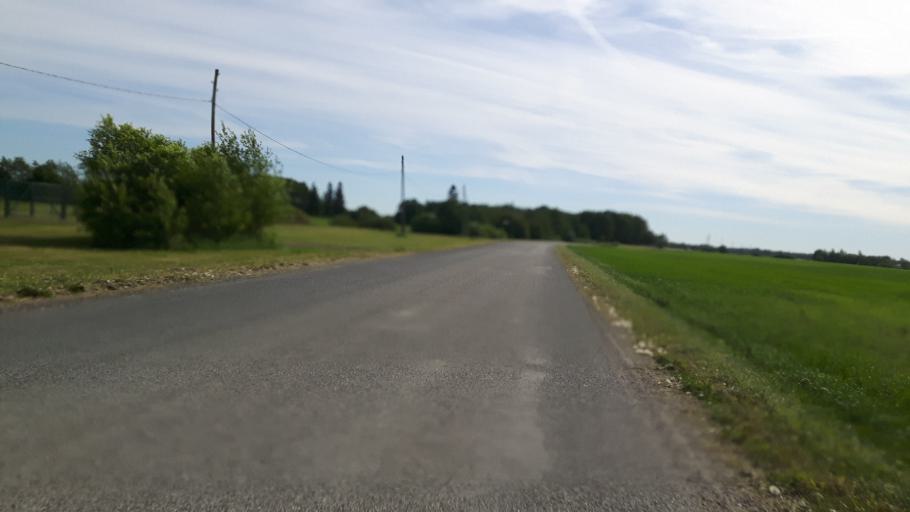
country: EE
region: Harju
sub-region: Raasiku vald
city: Arukula
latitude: 59.4261
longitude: 25.0906
